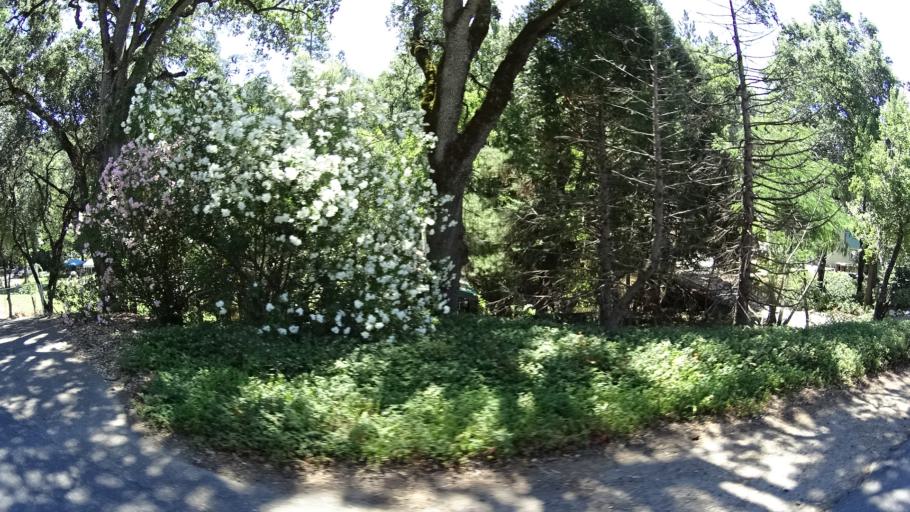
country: US
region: California
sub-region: Calaveras County
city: Murphys
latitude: 38.1142
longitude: -120.5033
